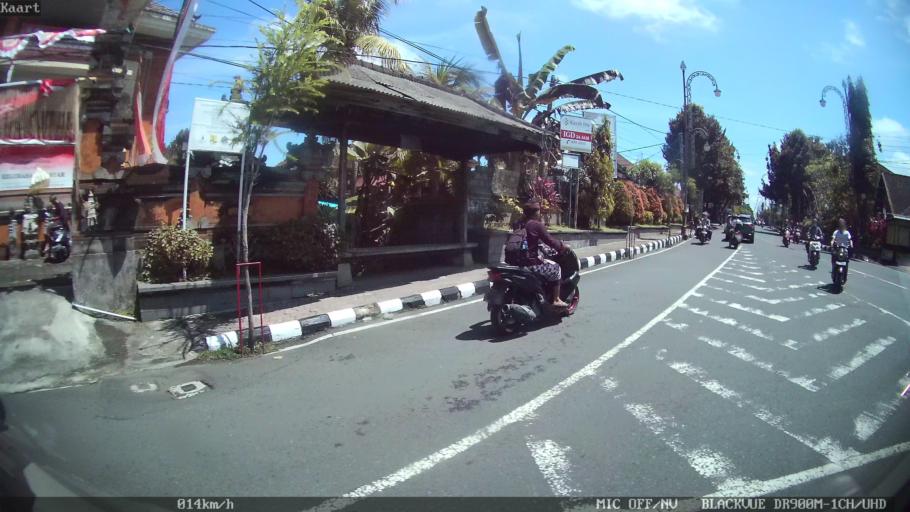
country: ID
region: Bali
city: Banjar Kelodan
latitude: -8.5419
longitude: 115.3321
